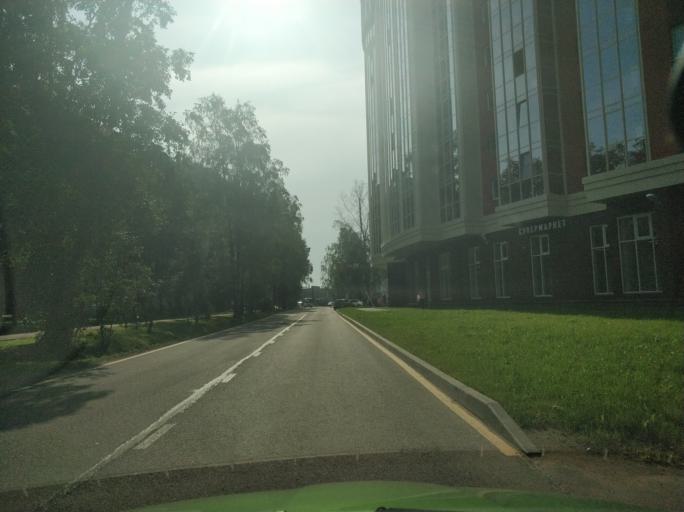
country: RU
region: Leningrad
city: Murino
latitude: 60.0433
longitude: 30.4639
